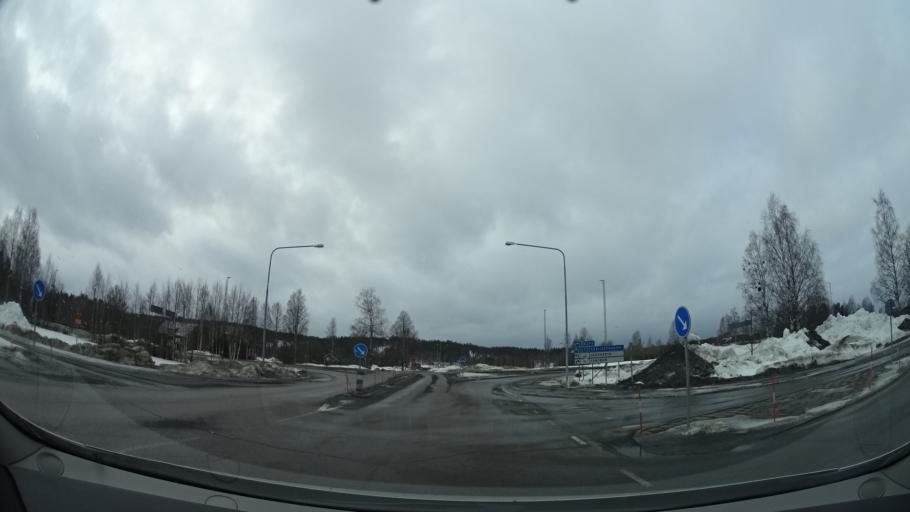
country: SE
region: Vaesterbotten
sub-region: Skelleftea Kommun
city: Skelleftea
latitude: 64.7466
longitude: 21.0143
